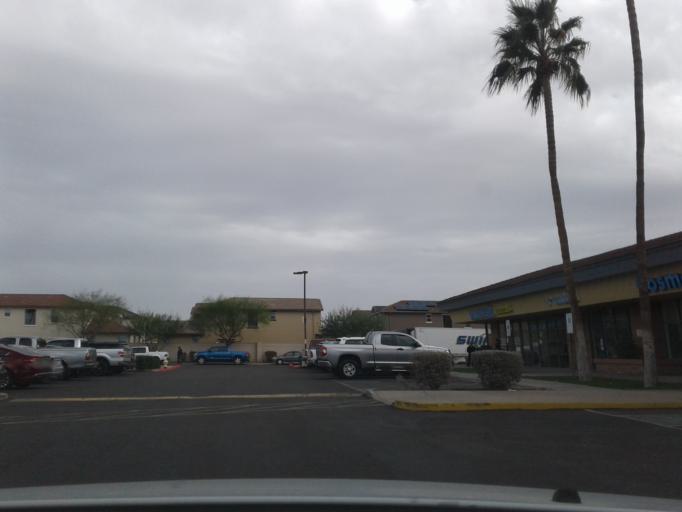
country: US
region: Arizona
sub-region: Maricopa County
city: Tolleson
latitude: 33.4795
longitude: -112.2179
